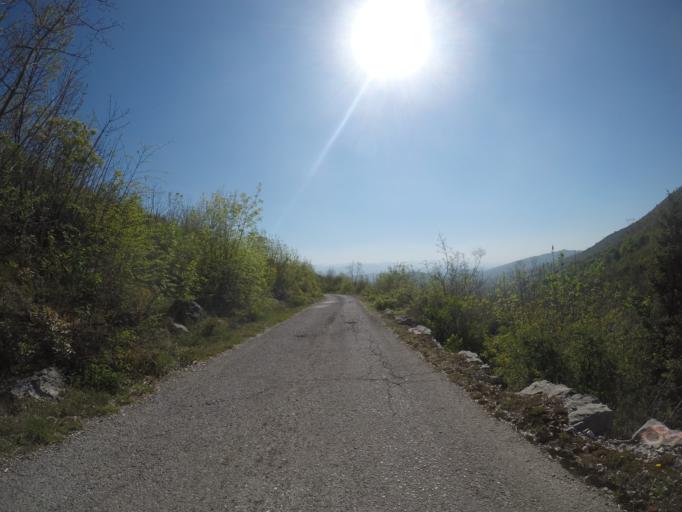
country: ME
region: Danilovgrad
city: Danilovgrad
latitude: 42.5141
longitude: 19.0655
